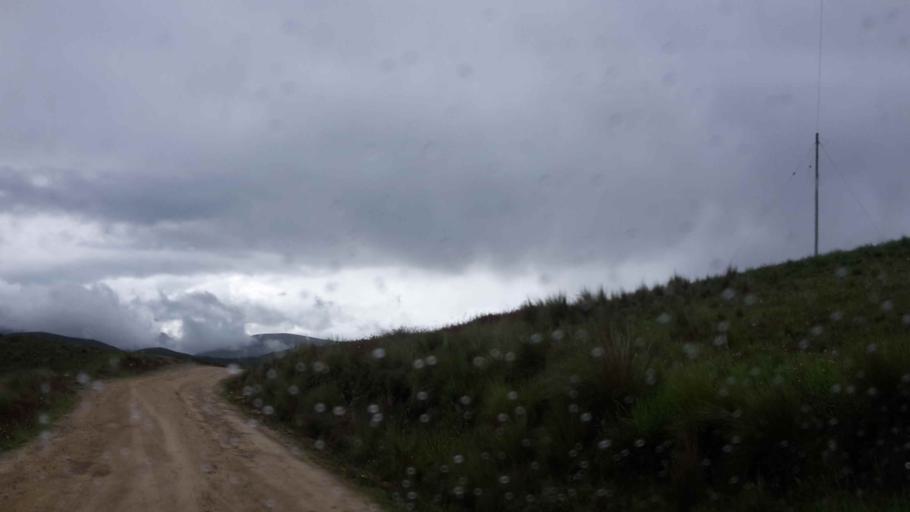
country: BO
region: Cochabamba
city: Cochabamba
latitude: -17.1456
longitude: -66.1021
